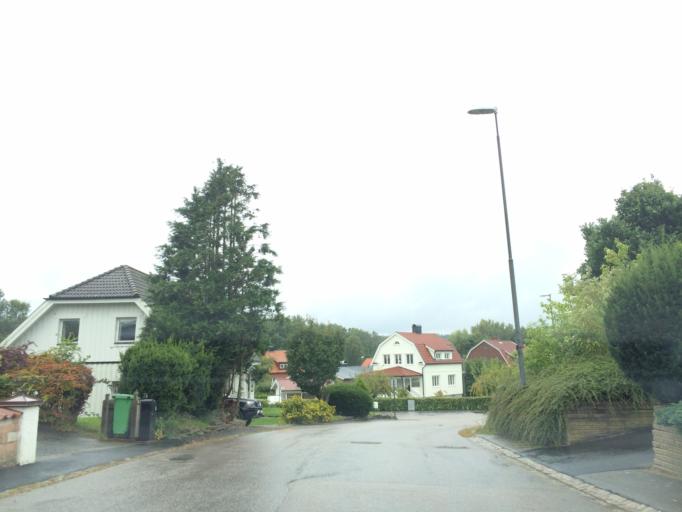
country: SE
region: Vaestra Goetaland
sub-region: Trollhattan
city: Trollhattan
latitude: 58.2800
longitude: 12.2645
